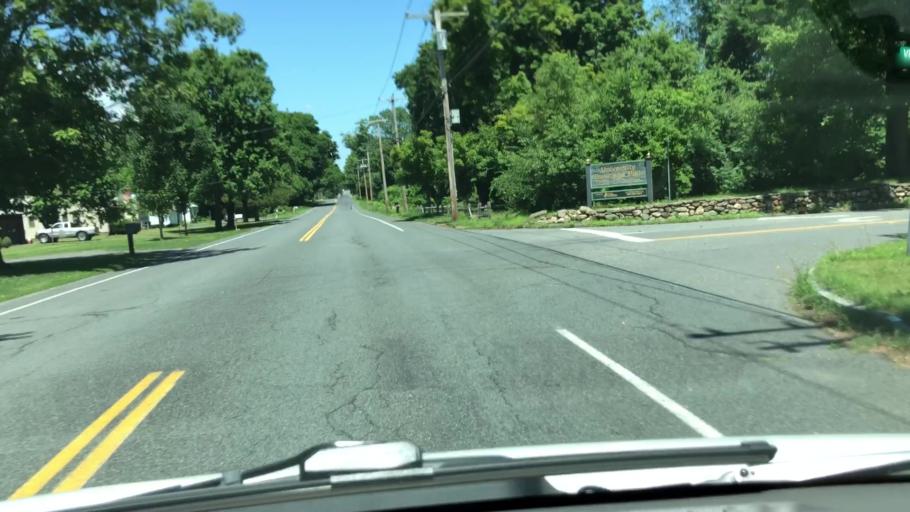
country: US
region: Massachusetts
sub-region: Hampshire County
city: Amherst Center
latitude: 42.3635
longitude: -72.5499
